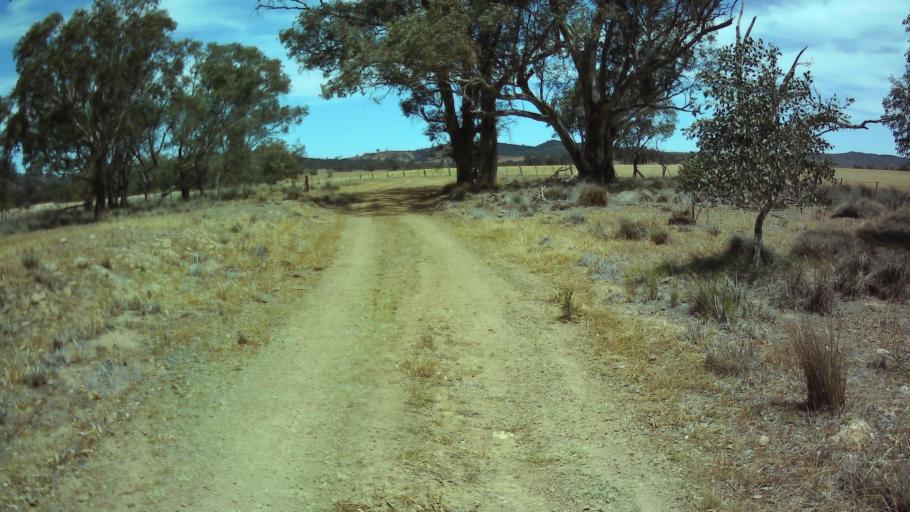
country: AU
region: New South Wales
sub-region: Weddin
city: Grenfell
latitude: -33.7608
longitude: 148.1454
